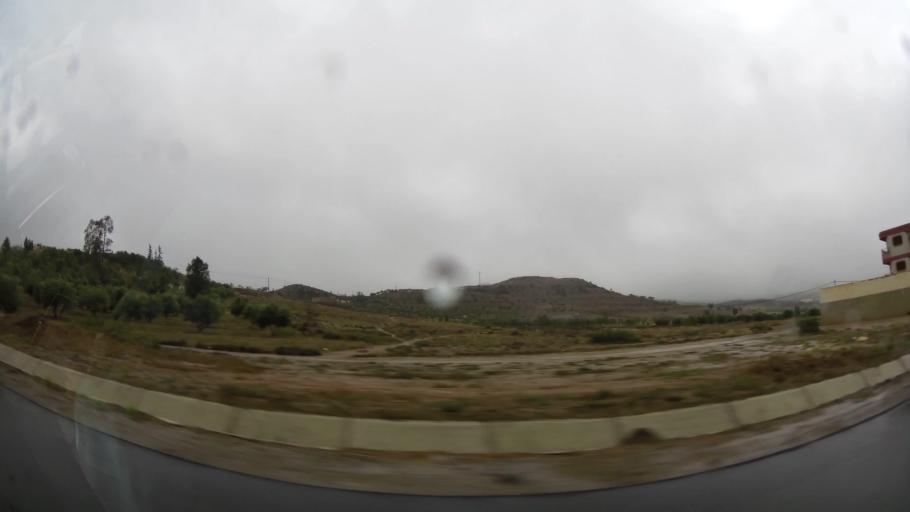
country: MA
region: Oriental
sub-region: Nador
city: Midar
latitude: 34.8305
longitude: -3.7195
